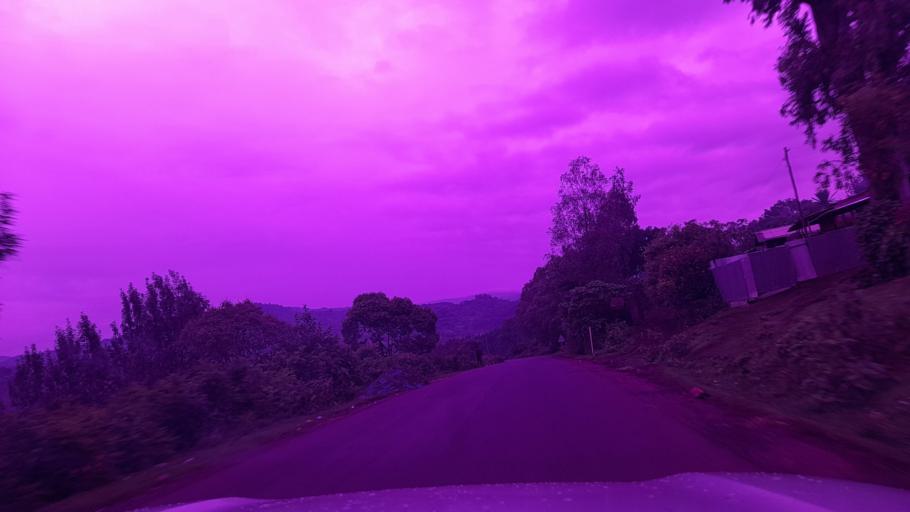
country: ET
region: Oromiya
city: Jima
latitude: 7.9295
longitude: 37.4290
